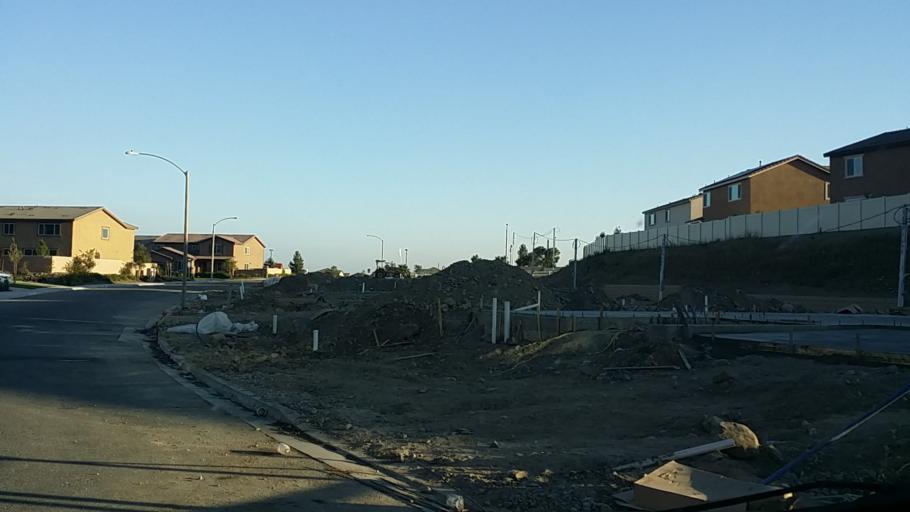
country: US
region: California
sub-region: San Bernardino County
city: Muscoy
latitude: 34.1907
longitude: -117.4148
